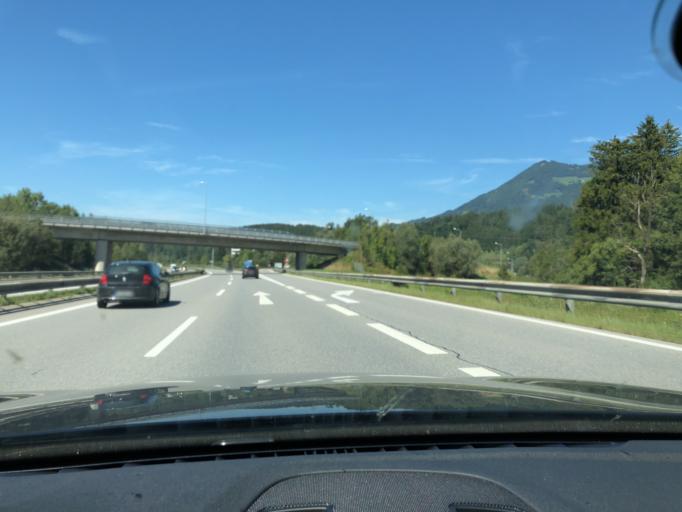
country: AT
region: Vorarlberg
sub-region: Politischer Bezirk Bludenz
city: Nenzing
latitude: 47.1902
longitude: 9.7189
